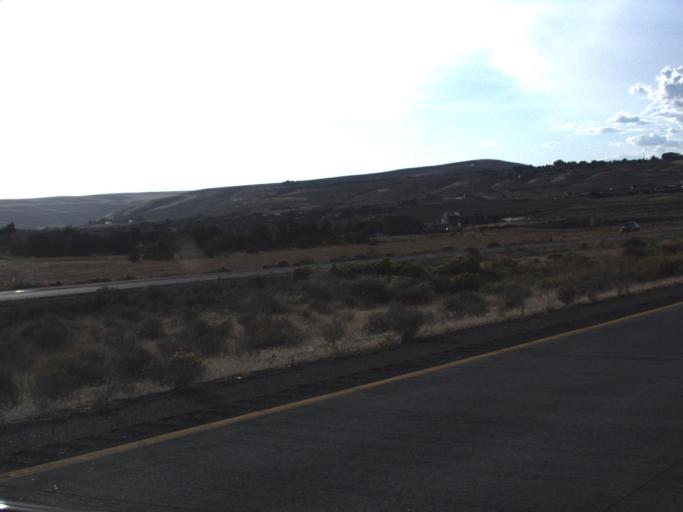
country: US
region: Washington
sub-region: Franklin County
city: West Pasco
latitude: 46.1906
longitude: -119.2606
